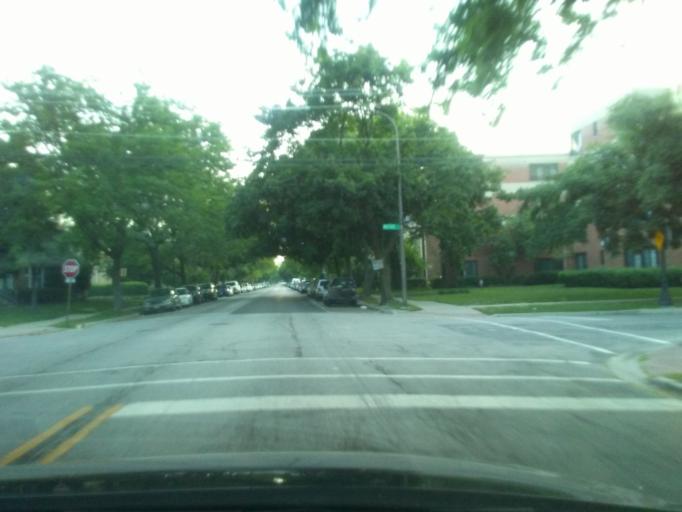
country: US
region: Illinois
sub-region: Cook County
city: Evanston
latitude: 42.0229
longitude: -87.6804
